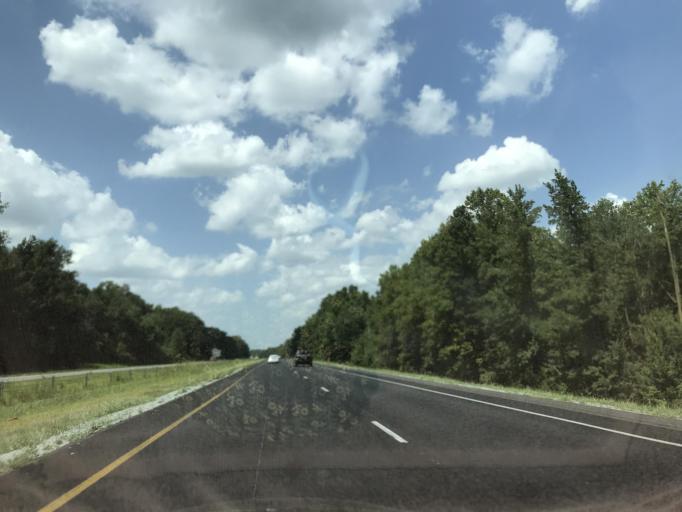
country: US
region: North Carolina
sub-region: Duplin County
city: Warsaw
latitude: 34.9377
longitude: -78.0534
